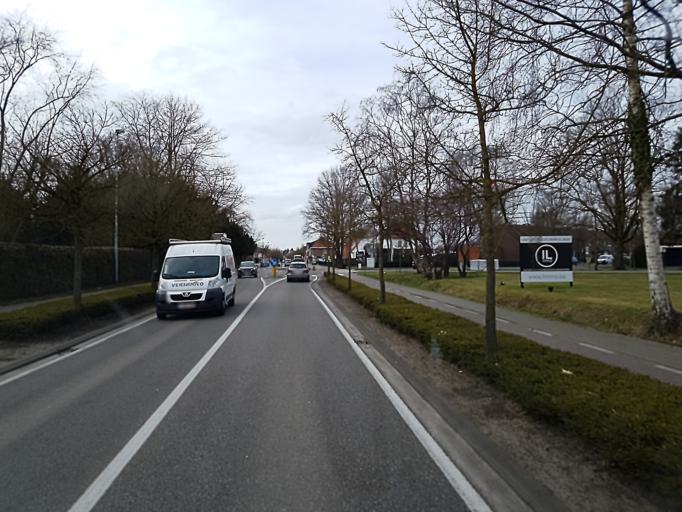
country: BE
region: Flanders
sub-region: Provincie Antwerpen
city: Oud-Turnhout
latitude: 51.3140
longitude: 4.9895
